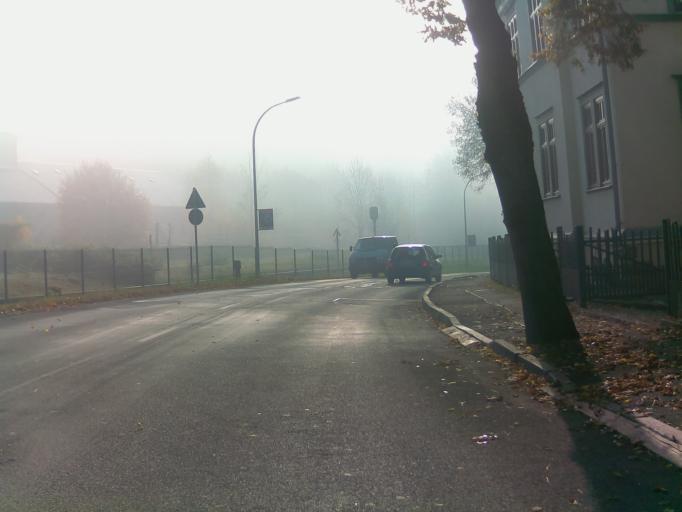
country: DE
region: Thuringia
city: Steinach
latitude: 50.4309
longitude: 11.1607
